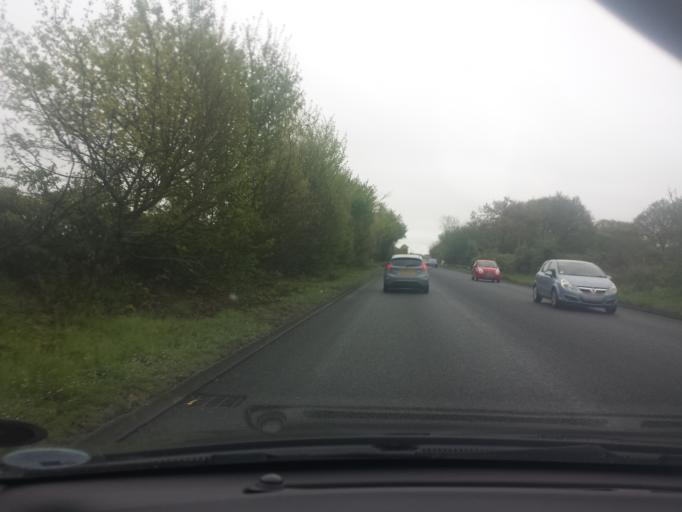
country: GB
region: England
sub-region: Essex
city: Little Clacton
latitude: 51.8306
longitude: 1.1295
